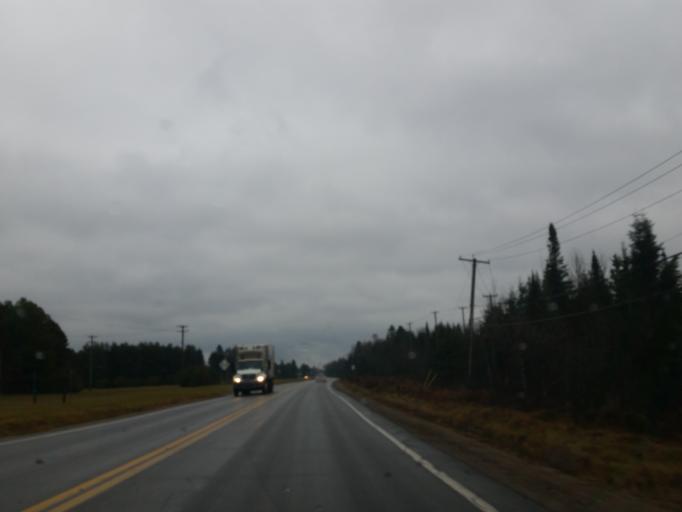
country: CA
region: Quebec
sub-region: Capitale-Nationale
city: Shannon
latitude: 46.8864
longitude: -71.5016
